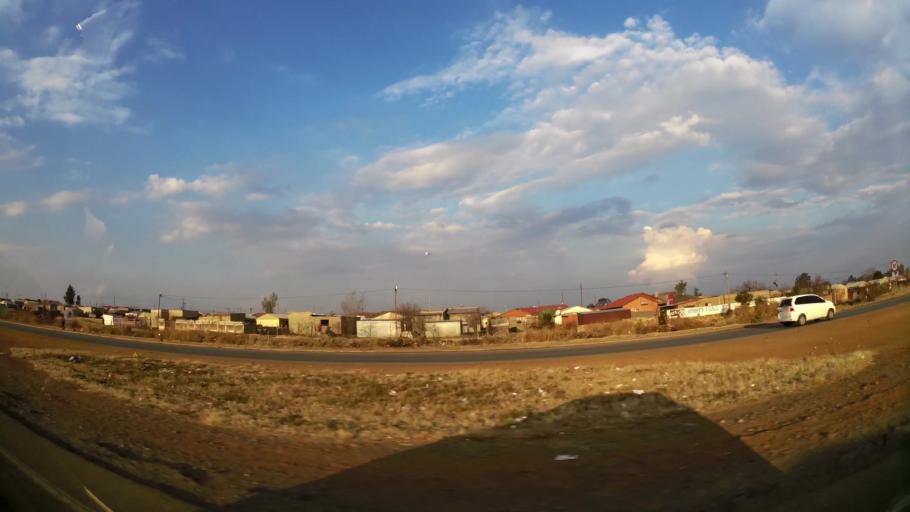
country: ZA
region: Gauteng
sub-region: Sedibeng District Municipality
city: Vanderbijlpark
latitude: -26.6030
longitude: 27.8177
